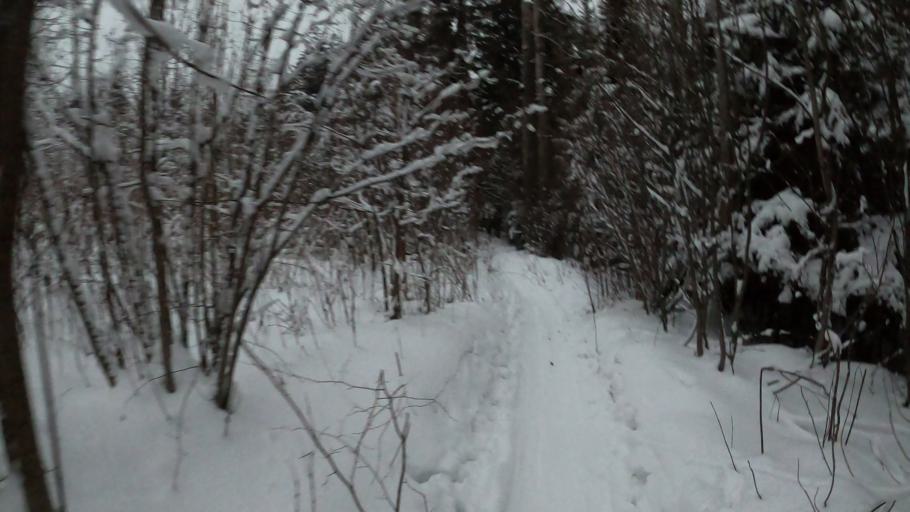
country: RU
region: Moskovskaya
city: Nakhabino
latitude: 55.8952
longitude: 37.2080
